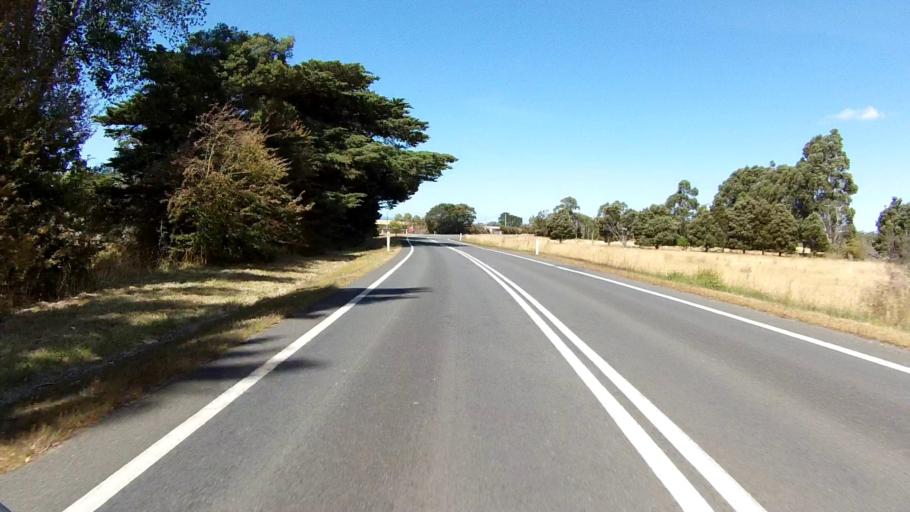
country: AU
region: Tasmania
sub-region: Break O'Day
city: St Helens
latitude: -42.0688
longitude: 148.0644
